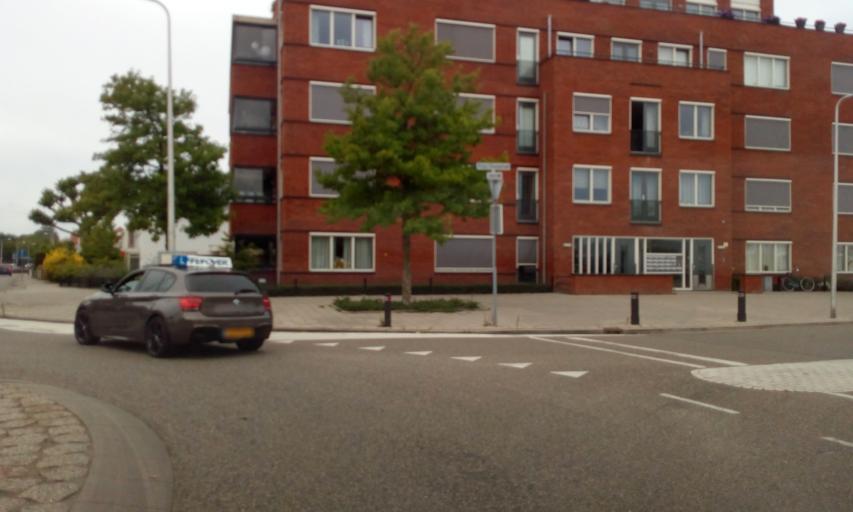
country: NL
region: South Holland
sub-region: Gemeente Westland
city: Kwintsheul
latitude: 52.0300
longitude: 4.2725
